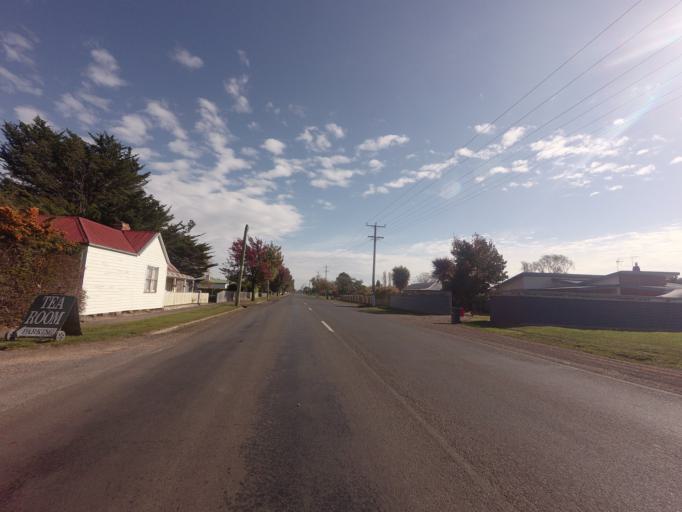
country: AU
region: Tasmania
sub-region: Meander Valley
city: Westbury
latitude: -41.5261
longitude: 146.8493
